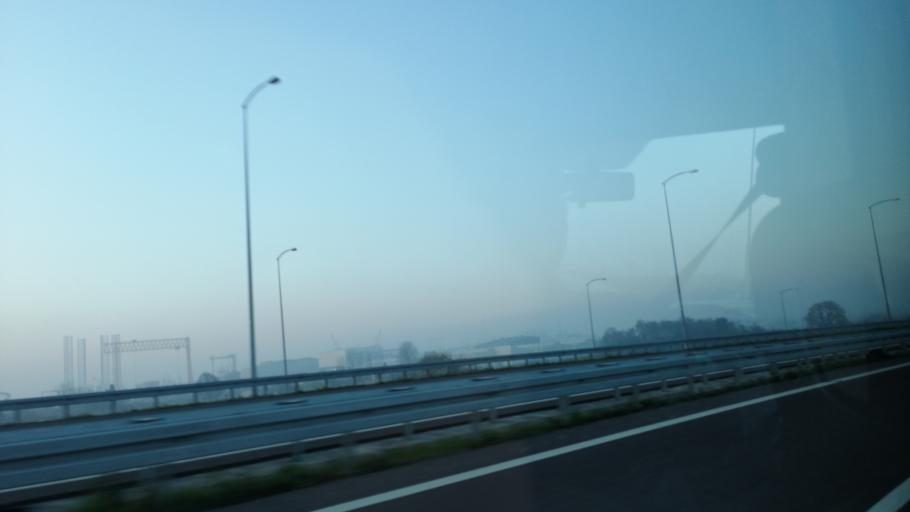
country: TR
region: Yalova
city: Altinova
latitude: 40.6949
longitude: 29.4709
